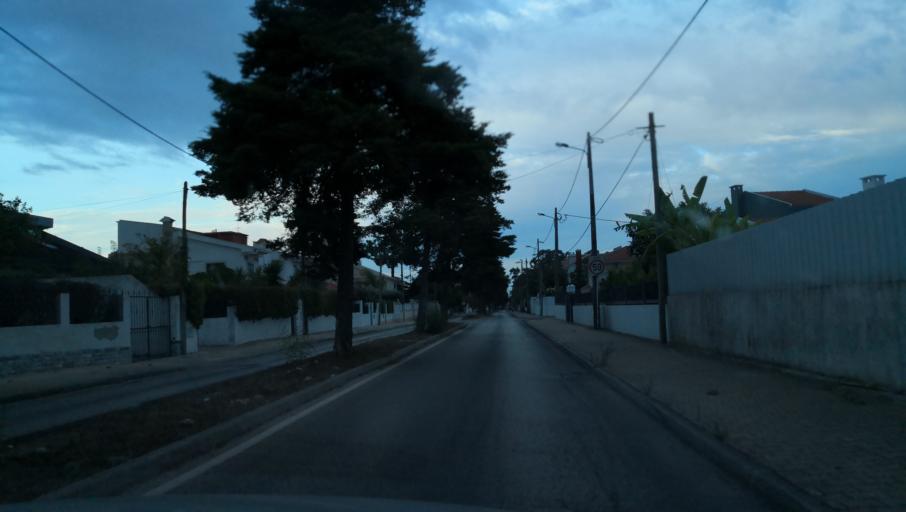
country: PT
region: Setubal
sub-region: Almada
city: Charneca
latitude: 38.6007
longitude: -9.1754
